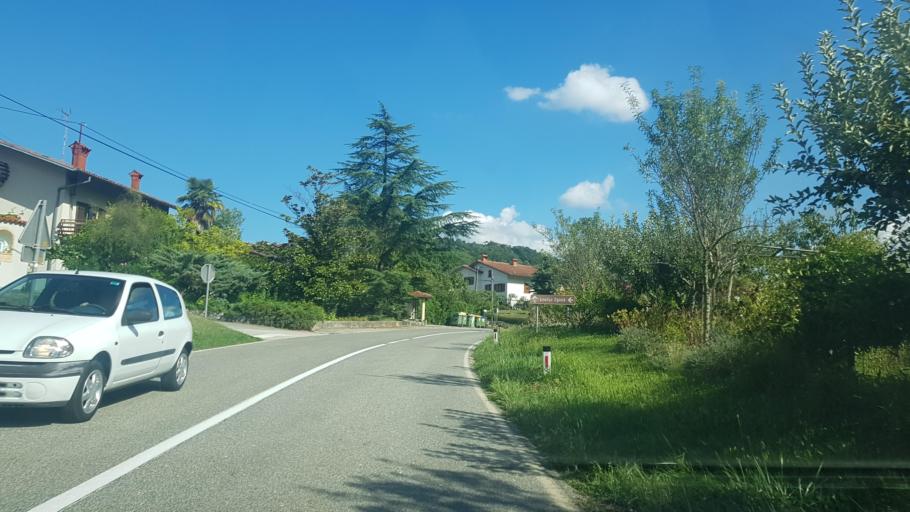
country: SI
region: Komen
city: Komen
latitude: 45.8670
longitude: 13.7787
